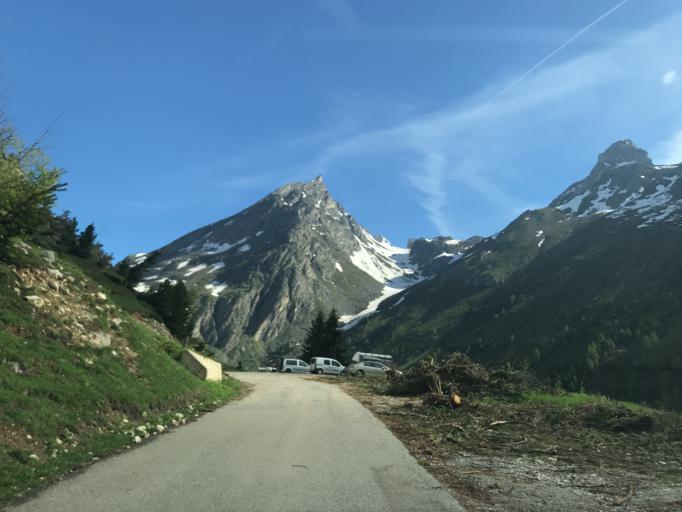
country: FR
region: Rhone-Alpes
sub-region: Departement de la Savoie
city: Modane
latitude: 45.2297
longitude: 6.6728
